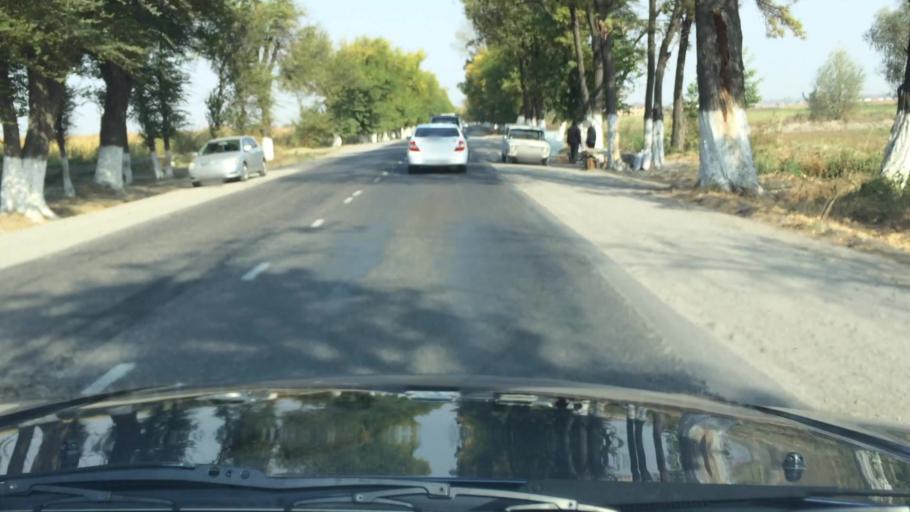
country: KG
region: Chuy
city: Lebedinovka
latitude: 42.9040
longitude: 74.6859
